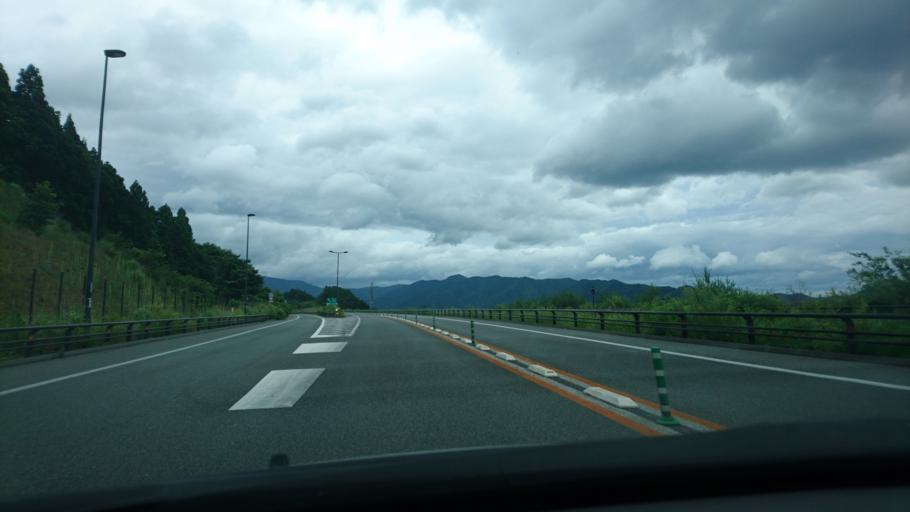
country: JP
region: Iwate
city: Ofunato
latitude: 39.0318
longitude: 141.7107
